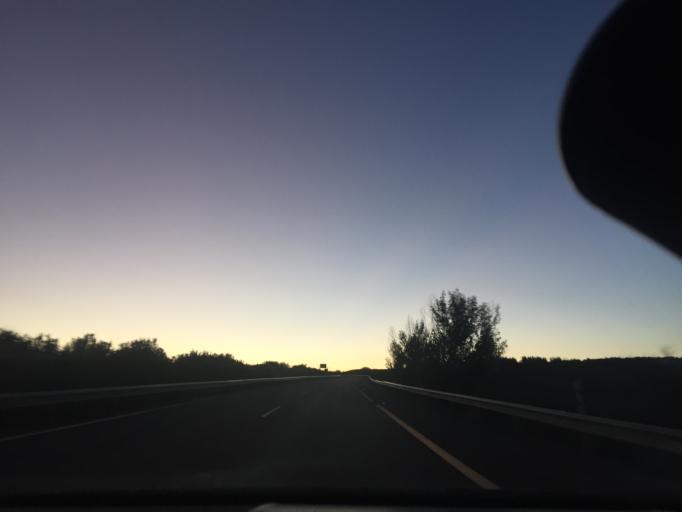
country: ES
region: Andalusia
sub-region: Provincia de Jaen
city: Jaen
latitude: 37.8064
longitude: -3.8040
